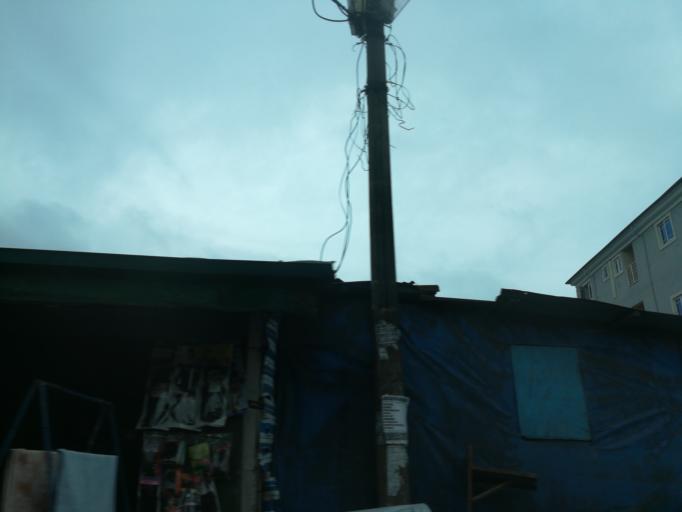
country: NG
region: Rivers
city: Port Harcourt
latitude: 4.8327
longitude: 7.0241
